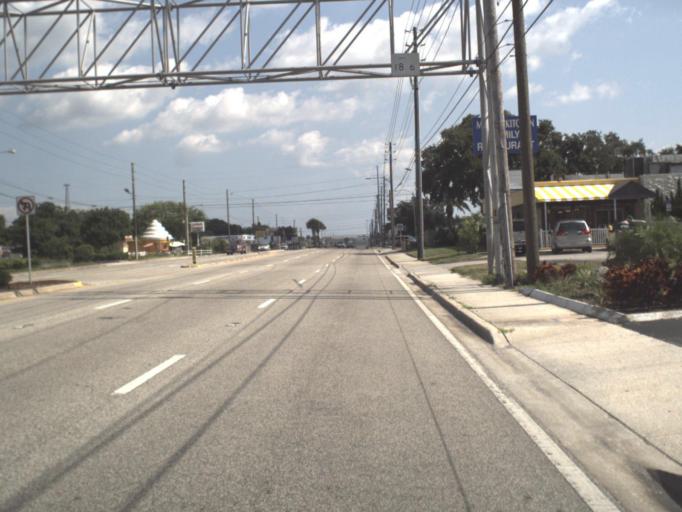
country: US
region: Florida
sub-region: Pinellas County
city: Bay Pines
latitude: 27.8249
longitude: -82.7869
